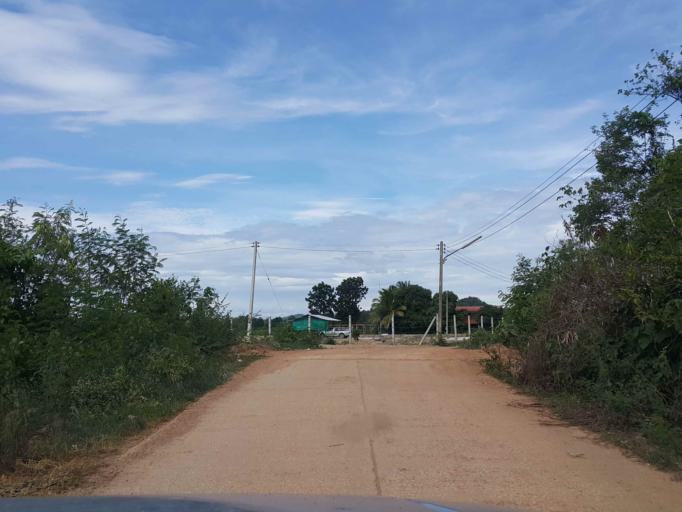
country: TH
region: Sukhothai
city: Ban Dan Lan Hoi
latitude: 17.1037
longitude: 99.4722
